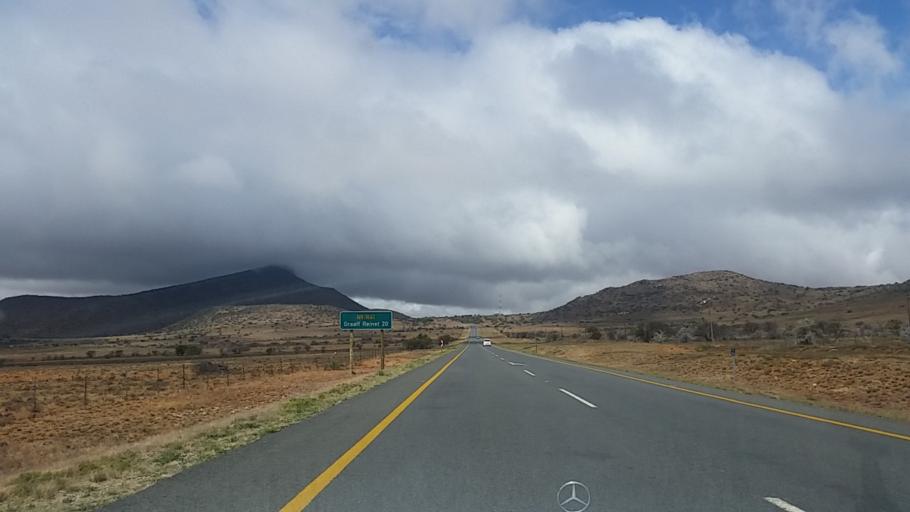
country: ZA
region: Eastern Cape
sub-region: Cacadu District Municipality
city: Graaff-Reinet
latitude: -32.0946
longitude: 24.6042
